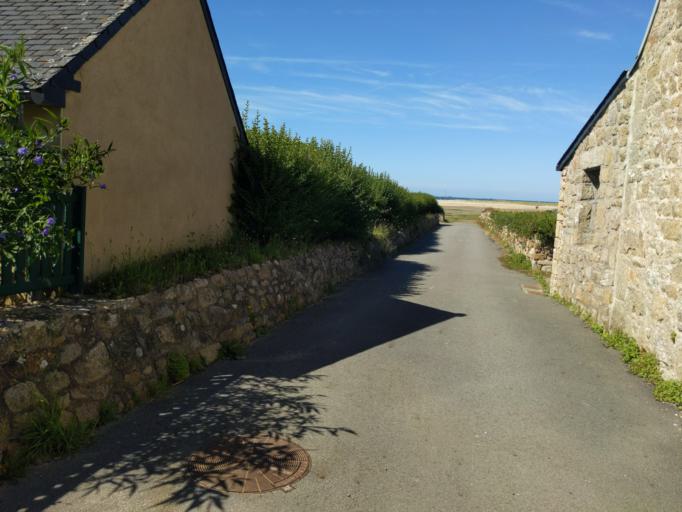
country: FR
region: Brittany
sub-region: Departement des Cotes-d'Armor
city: Pleubian
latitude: 48.8654
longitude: -3.0965
